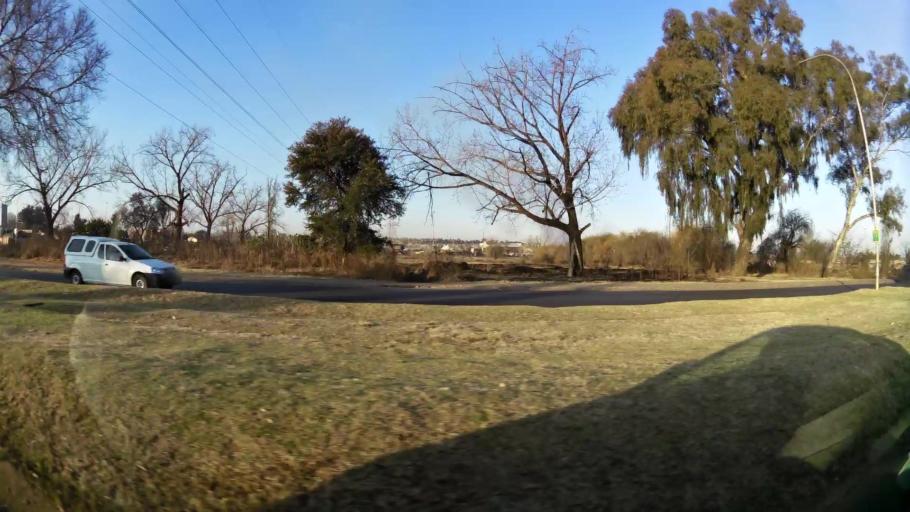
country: ZA
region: Gauteng
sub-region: City of Johannesburg Metropolitan Municipality
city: Soweto
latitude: -26.2395
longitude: 27.8792
